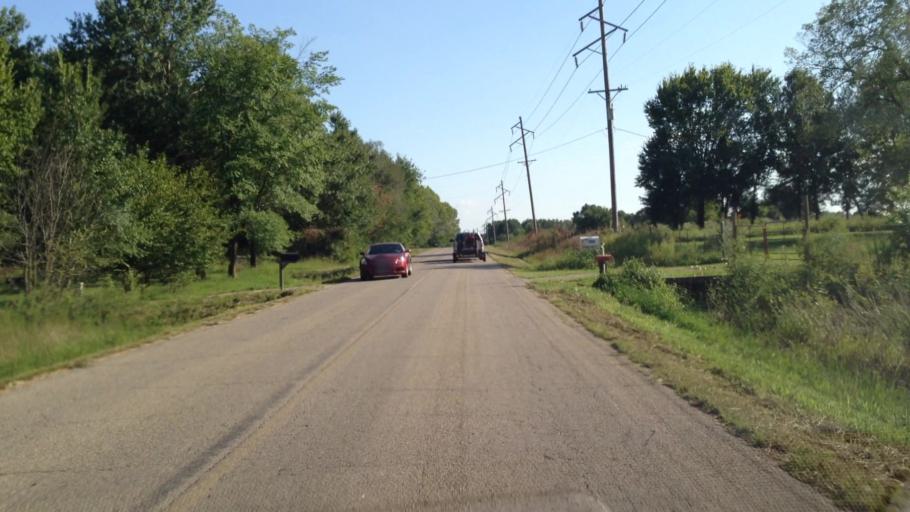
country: US
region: Kansas
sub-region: Crawford County
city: Frontenac
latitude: 37.4537
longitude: -94.6309
